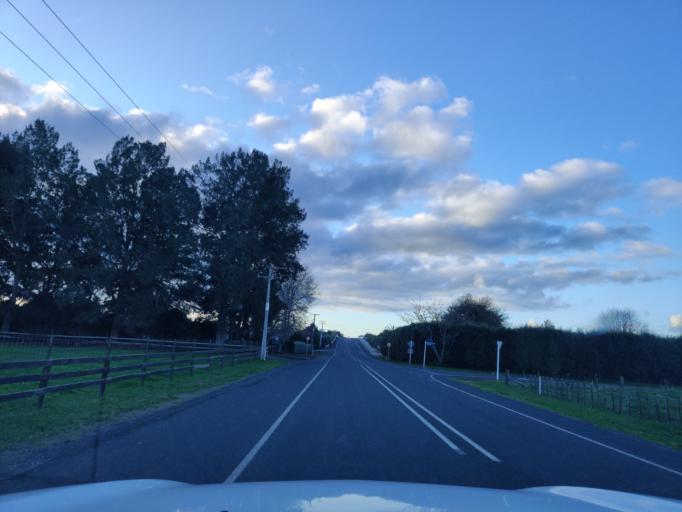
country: NZ
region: Waikato
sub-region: Waipa District
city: Cambridge
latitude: -37.8716
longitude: 175.4389
